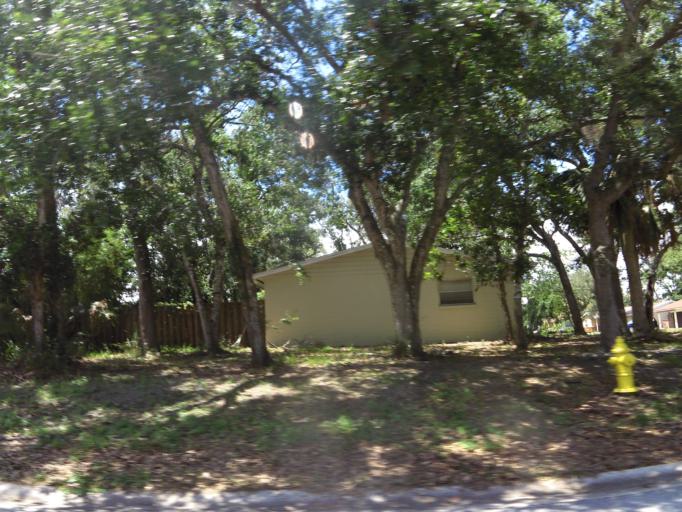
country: US
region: Florida
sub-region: Volusia County
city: Ormond Beach
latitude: 29.3094
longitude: -81.0688
